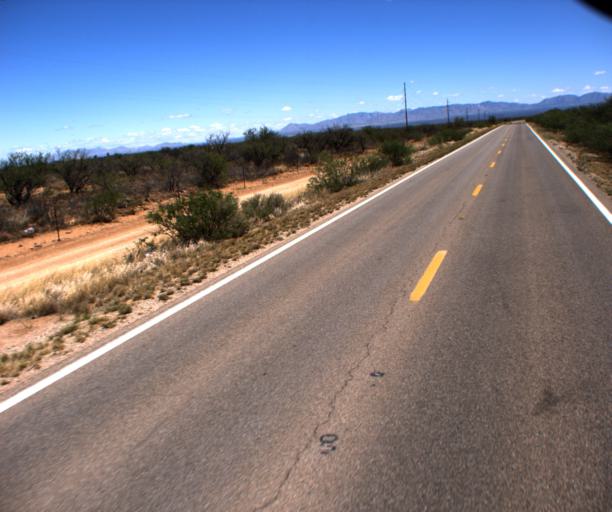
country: US
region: Arizona
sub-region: Cochise County
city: Huachuca City
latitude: 31.7049
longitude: -110.2884
